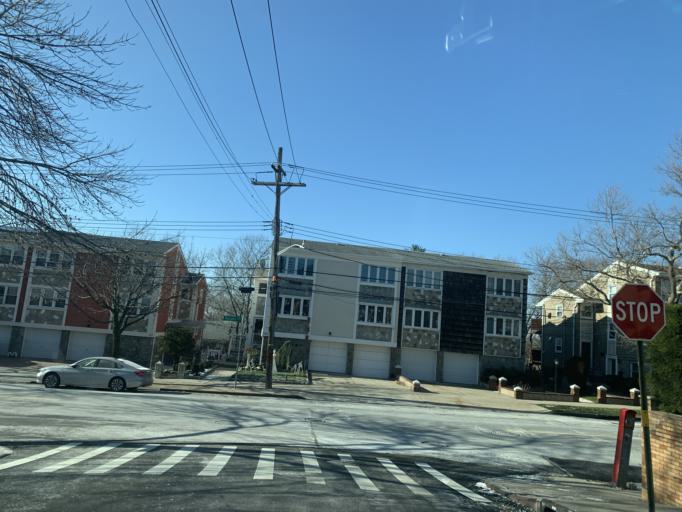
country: US
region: New York
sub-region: Nassau County
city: East Atlantic Beach
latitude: 40.7833
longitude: -73.8211
